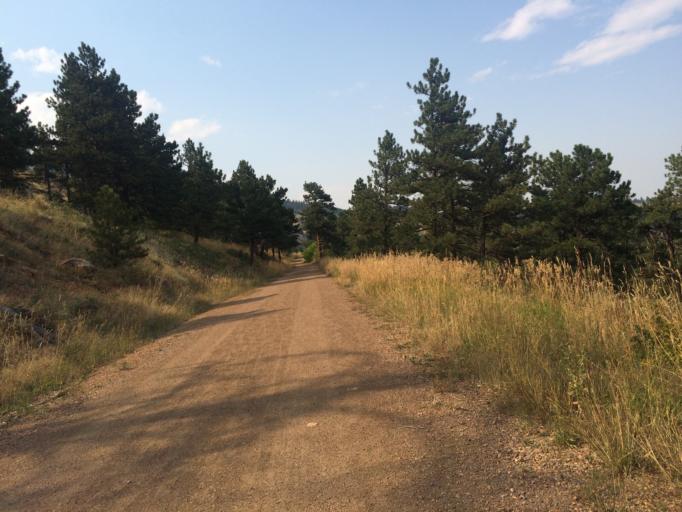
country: US
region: Colorado
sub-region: Boulder County
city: Boulder
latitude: 39.9292
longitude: -105.2740
